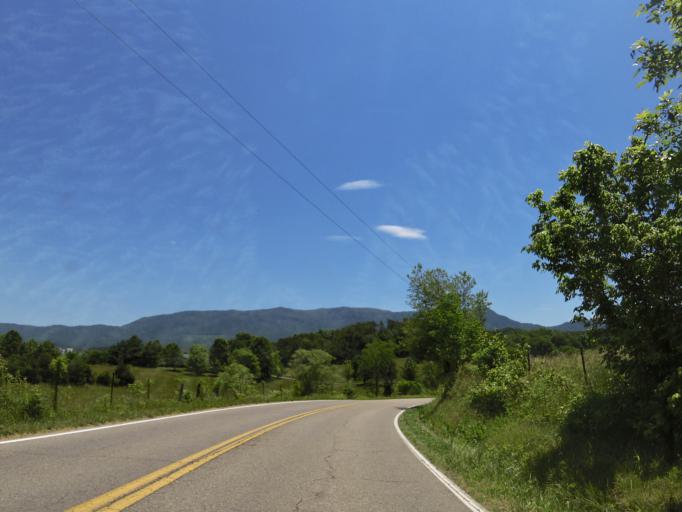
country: US
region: Tennessee
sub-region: Jefferson County
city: Dandridge
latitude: 35.9346
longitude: -83.3565
